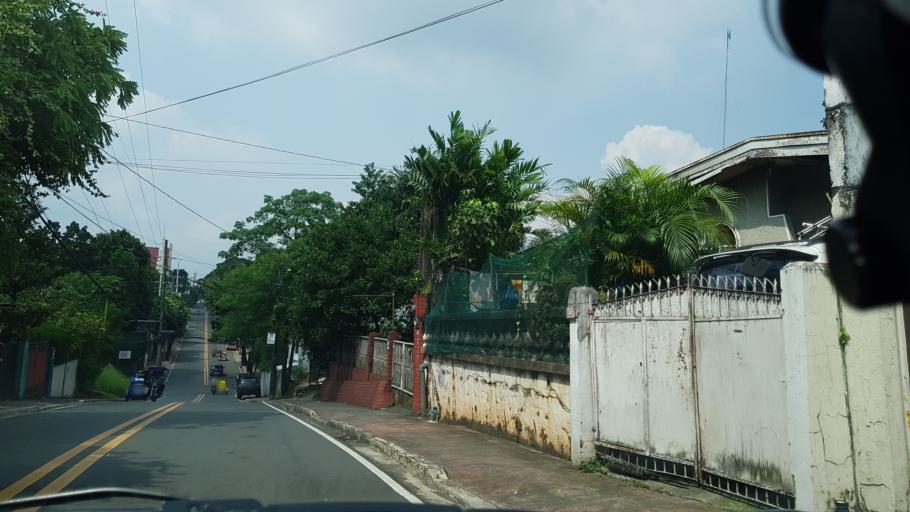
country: PH
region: Calabarzon
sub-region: Province of Rizal
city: Antipolo
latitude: 14.6564
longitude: 121.1182
